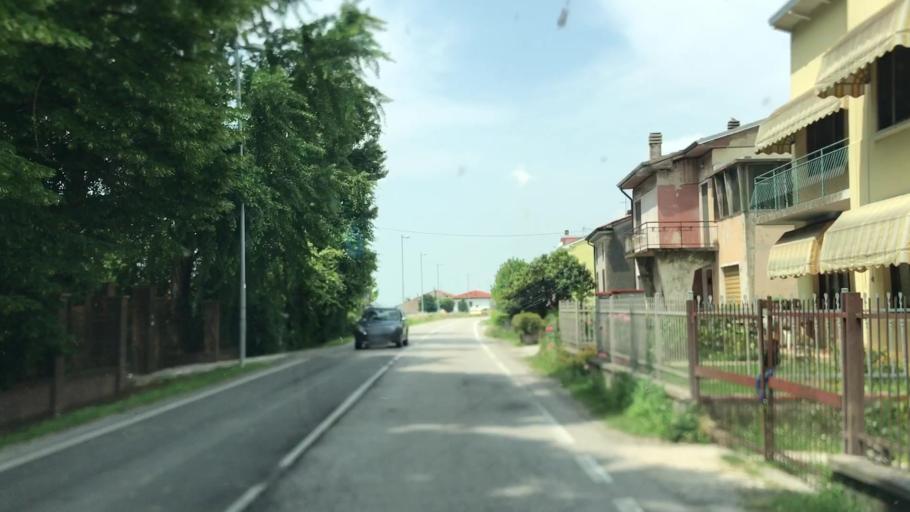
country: IT
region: Lombardy
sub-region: Provincia di Mantova
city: Carbonara di Po
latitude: 45.0380
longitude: 11.2227
